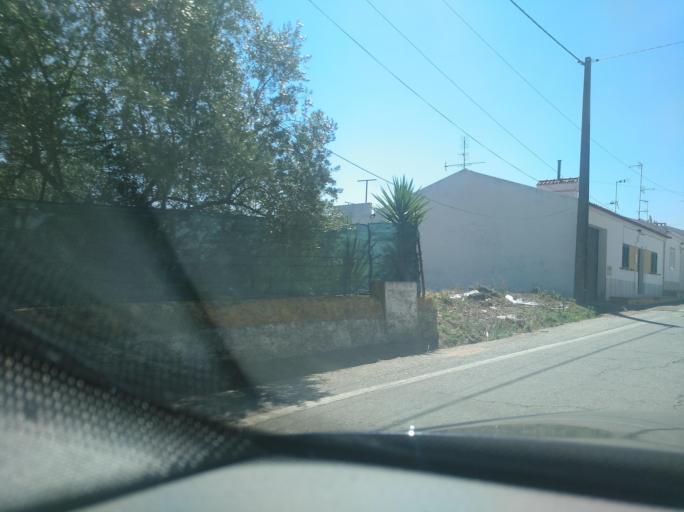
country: PT
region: Portalegre
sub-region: Arronches
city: Arronches
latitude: 38.9636
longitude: -7.3002
